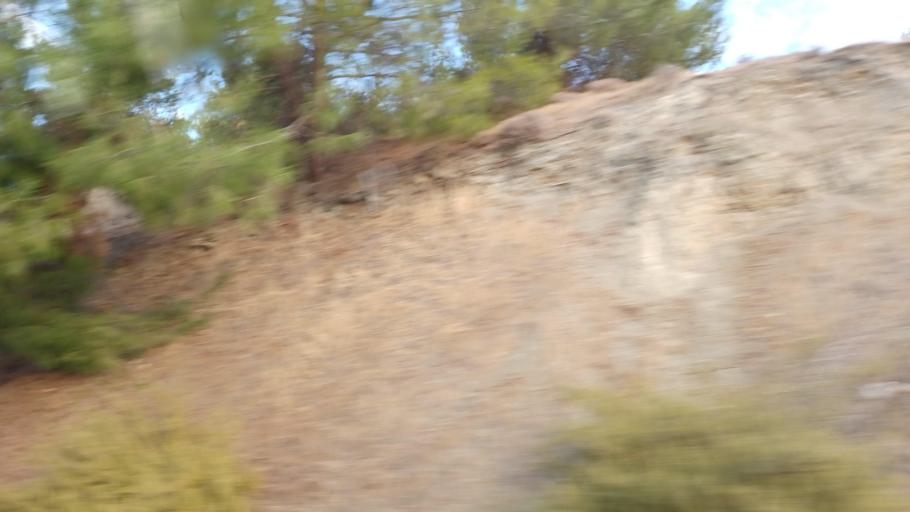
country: CY
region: Lefkosia
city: Kakopetria
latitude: 35.0341
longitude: 32.9018
